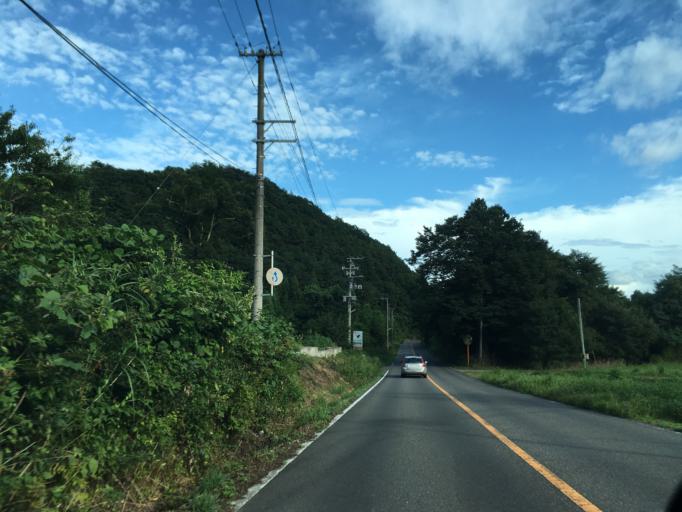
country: JP
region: Fukushima
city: Motomiya
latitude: 37.5108
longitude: 140.2717
